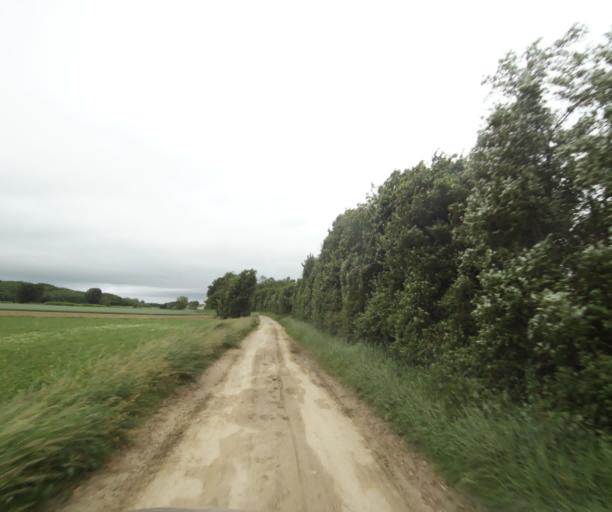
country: FR
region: Rhone-Alpes
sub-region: Departement de l'Ain
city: Miribel
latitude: 45.8460
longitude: 4.9252
